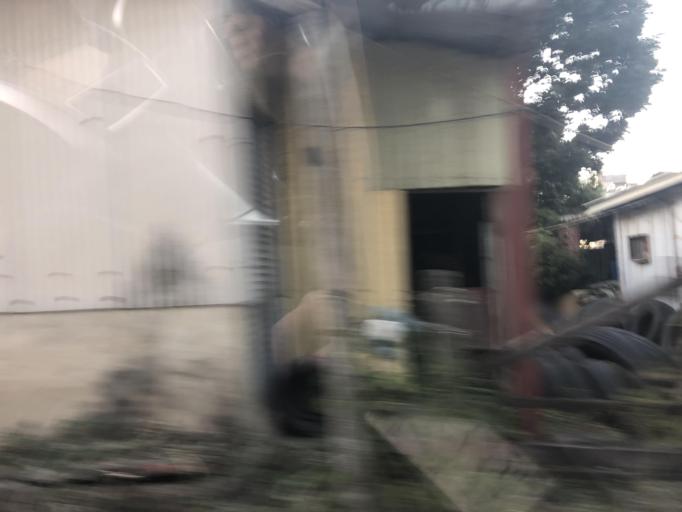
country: TW
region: Taiwan
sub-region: Tainan
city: Tainan
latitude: 23.0424
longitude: 120.2475
